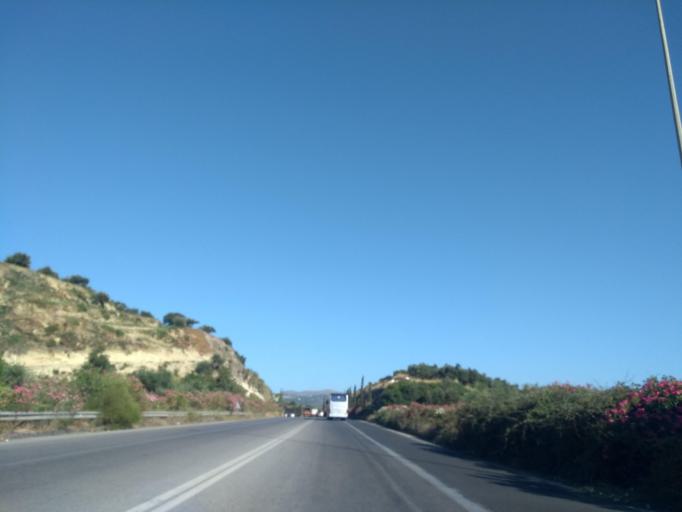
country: GR
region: Crete
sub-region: Nomos Chanias
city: Kolympari
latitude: 35.5221
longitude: 23.8140
